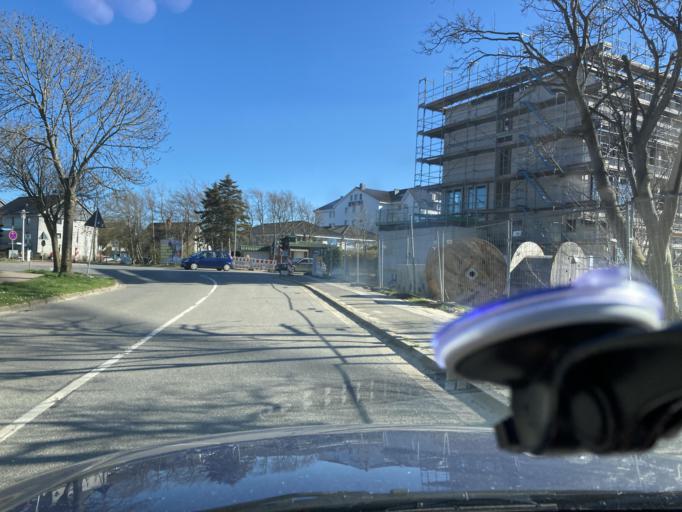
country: DE
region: Schleswig-Holstein
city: Busum
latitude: 54.1358
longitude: 8.8458
